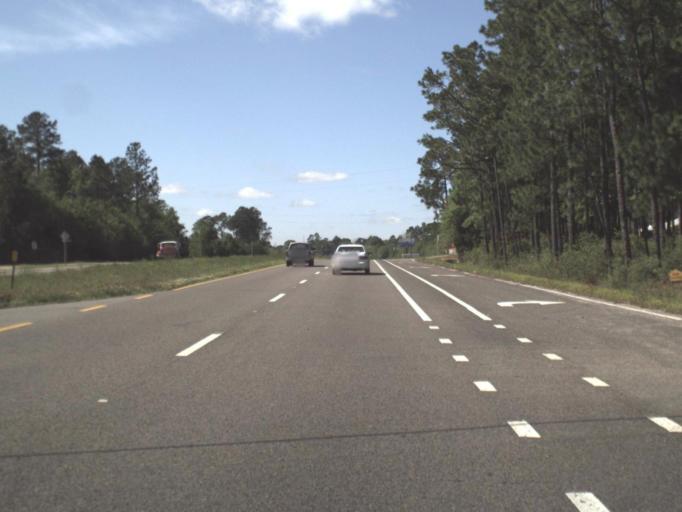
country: US
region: Florida
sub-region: Escambia County
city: Cantonment
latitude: 30.6217
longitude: -87.3268
